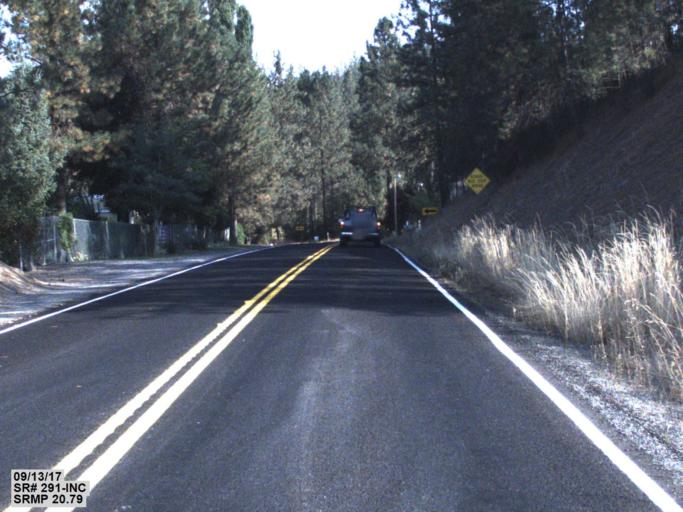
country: US
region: Washington
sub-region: Spokane County
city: Deer Park
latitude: 47.8914
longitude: -117.6600
